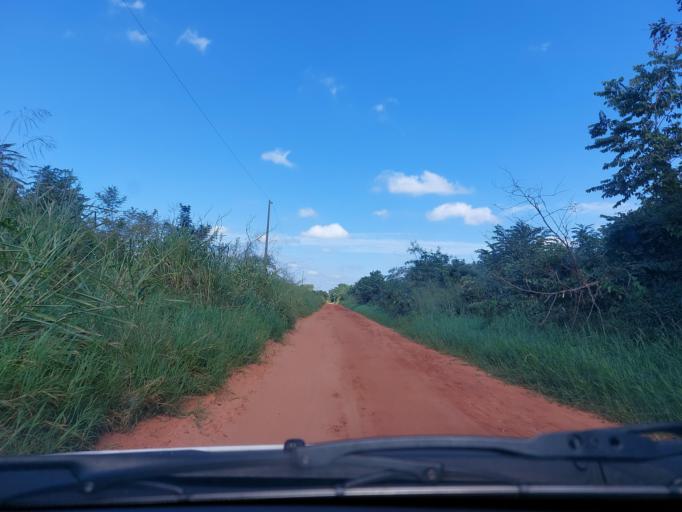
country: PY
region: San Pedro
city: Itacurubi del Rosario
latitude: -24.5316
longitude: -56.5655
